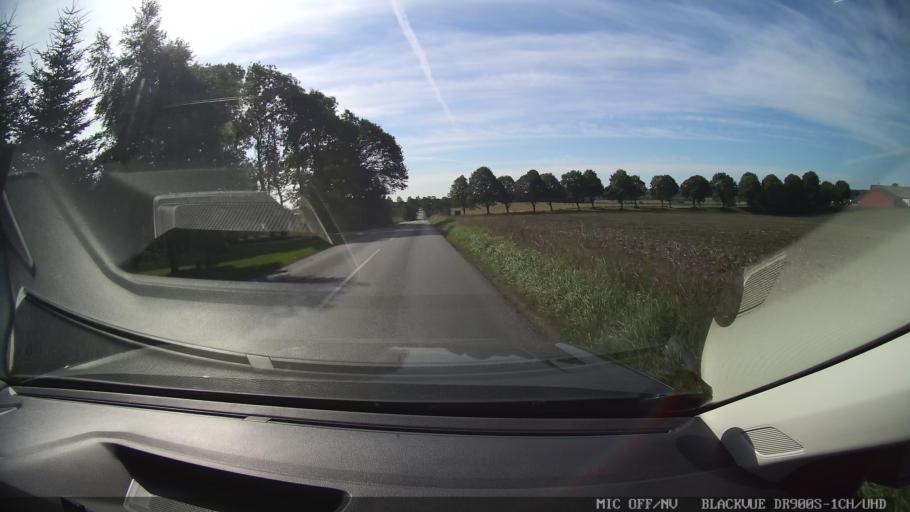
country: DK
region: North Denmark
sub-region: Mariagerfjord Kommune
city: Hobro
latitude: 56.5572
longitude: 9.8434
